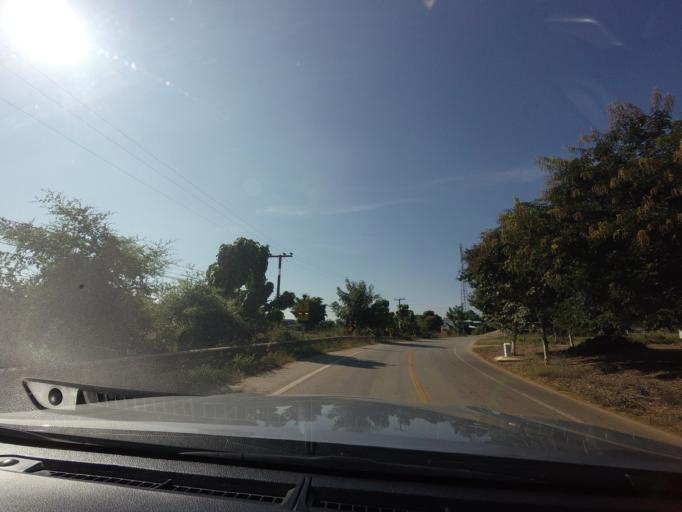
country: TH
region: Sukhothai
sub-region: Amphoe Si Satchanalai
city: Si Satchanalai
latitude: 17.6951
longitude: 99.7048
